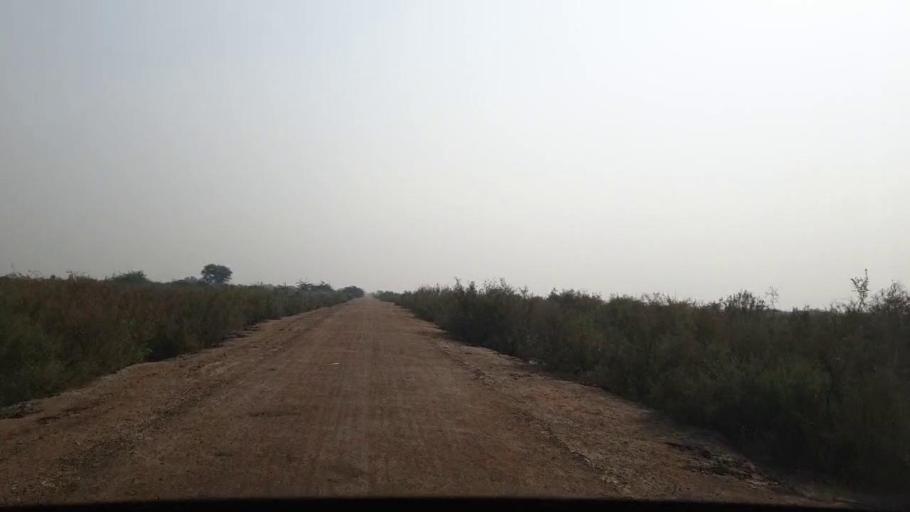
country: PK
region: Sindh
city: Jati
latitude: 24.2722
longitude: 68.4233
